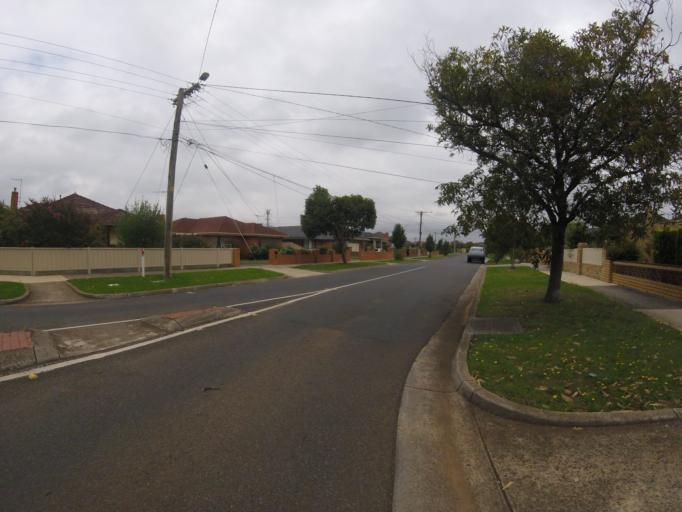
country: AU
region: Victoria
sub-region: Darebin
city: Reservoir
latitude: -37.7038
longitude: 145.0003
